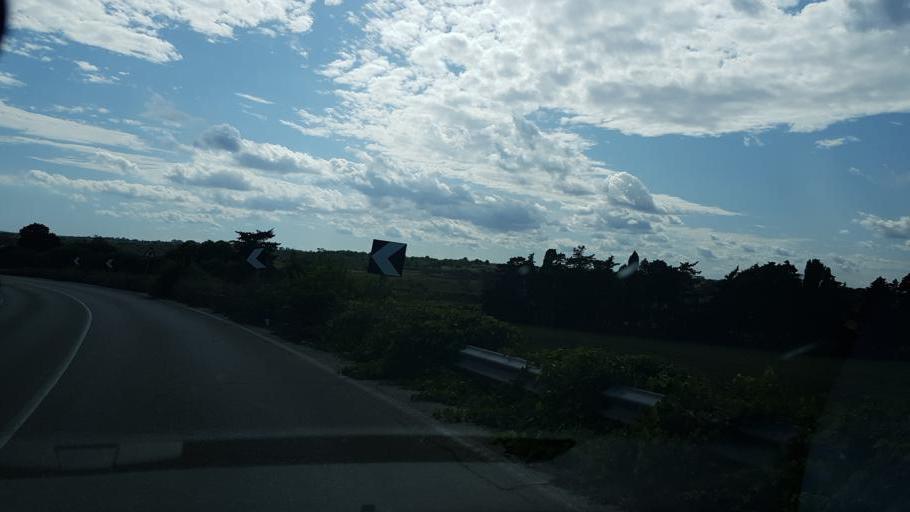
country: IT
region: Apulia
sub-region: Provincia di Lecce
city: Borgagne
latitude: 40.2245
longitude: 18.4410
